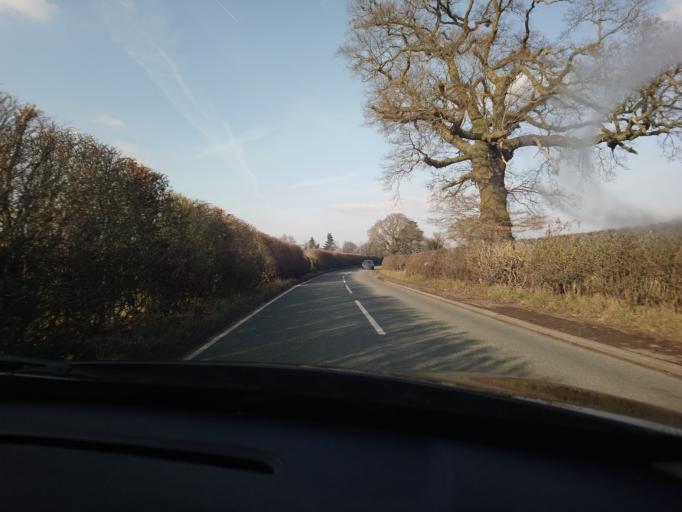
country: GB
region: England
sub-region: Shropshire
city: Bicton
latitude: 52.7498
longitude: -2.7800
